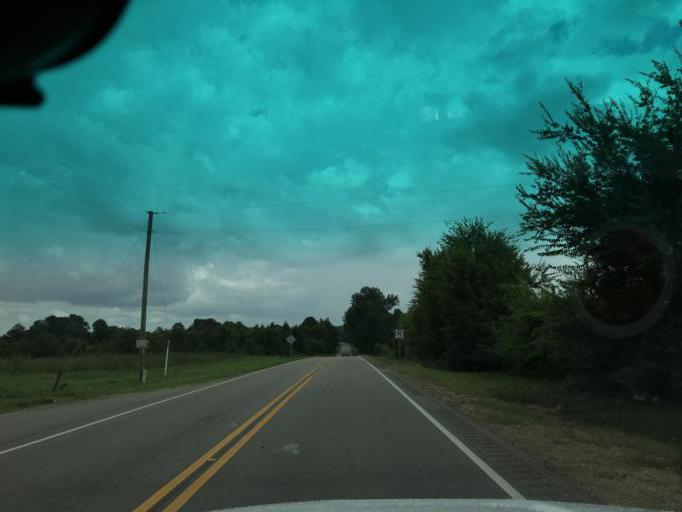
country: US
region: Alabama
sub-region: Montgomery County
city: Pike Road
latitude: 32.3655
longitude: -86.1113
